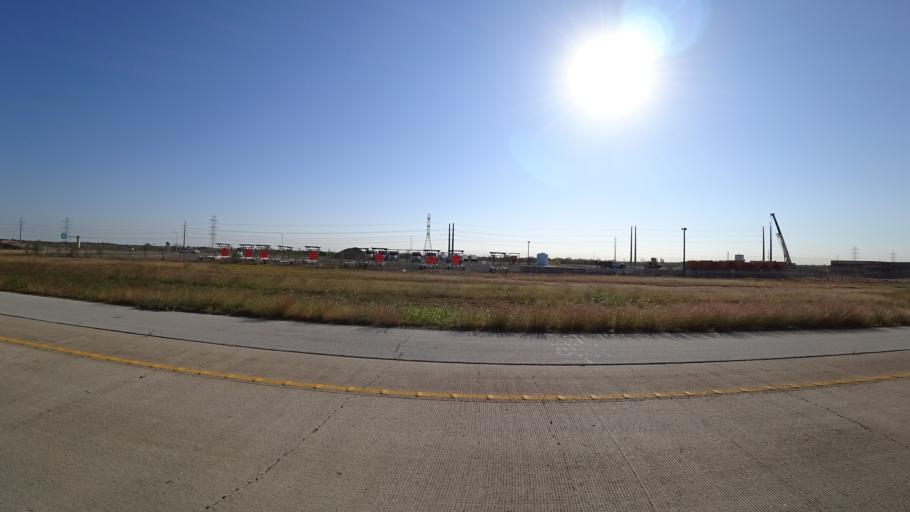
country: US
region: Texas
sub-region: Travis County
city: Hornsby Bend
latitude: 30.2379
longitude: -97.6166
